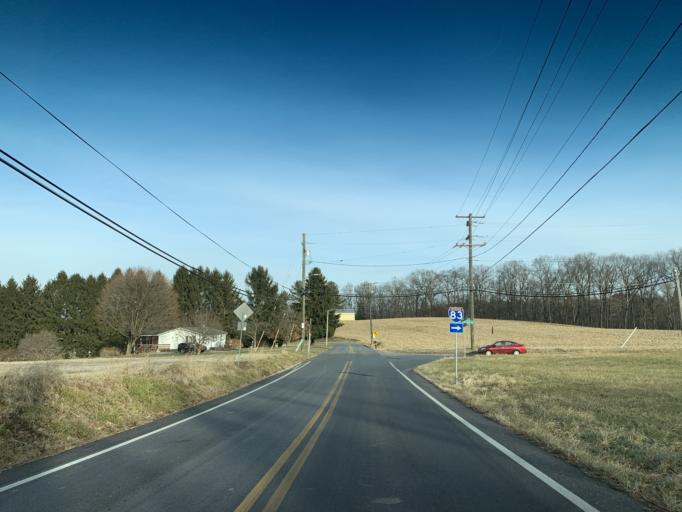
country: US
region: Maryland
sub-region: Carroll County
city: Hampstead
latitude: 39.6127
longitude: -76.8000
